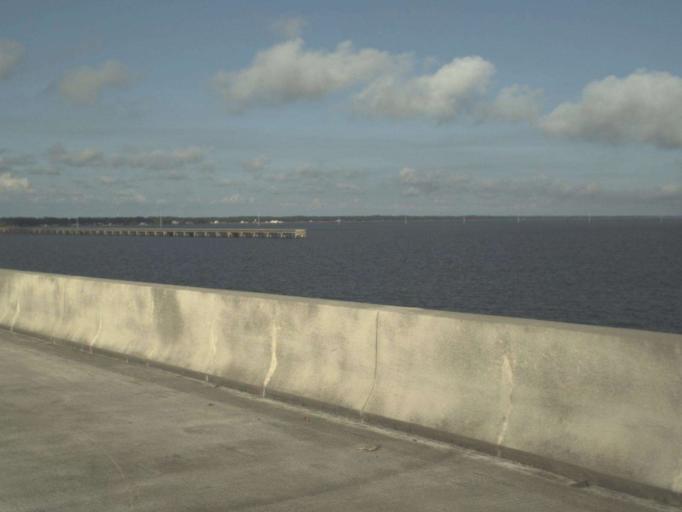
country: US
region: Florida
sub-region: Franklin County
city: Eastpoint
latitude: 29.7090
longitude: -84.8907
